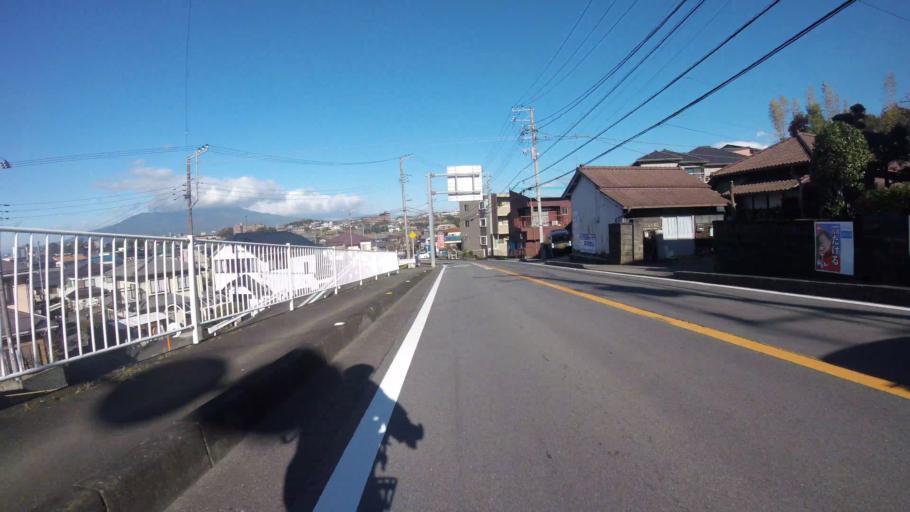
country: JP
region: Shizuoka
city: Mishima
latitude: 35.1214
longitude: 138.9302
